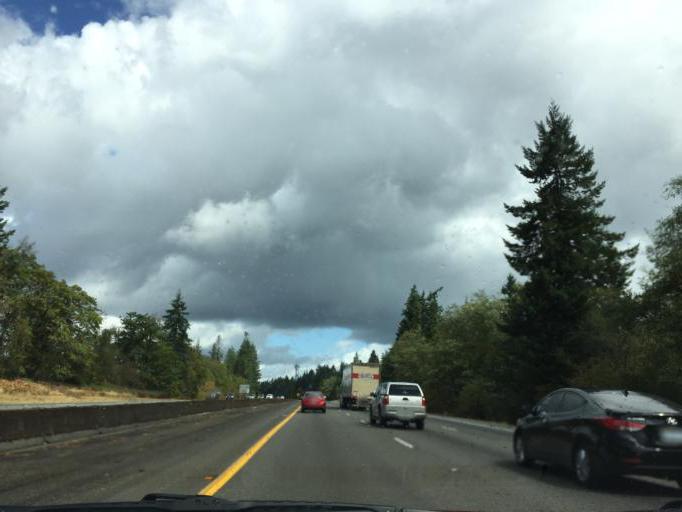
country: US
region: Washington
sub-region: Lewis County
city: Winlock
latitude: 46.4888
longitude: -122.8783
